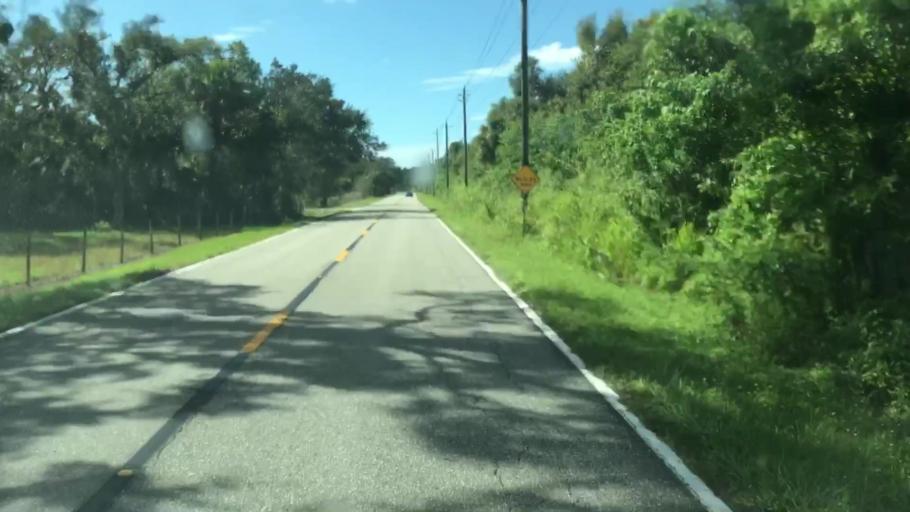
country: US
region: Florida
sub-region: Lee County
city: Alva
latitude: 26.7261
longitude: -81.6436
